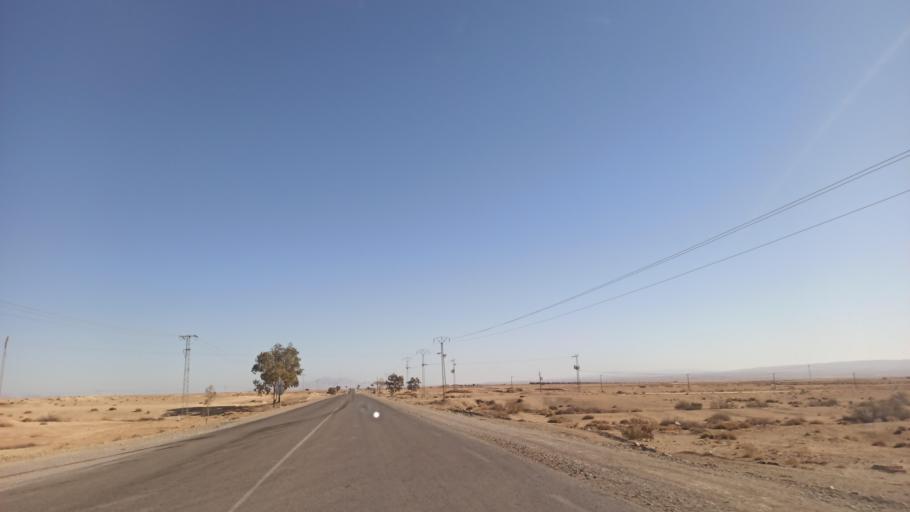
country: TN
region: Gafsa
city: Al Metlaoui
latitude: 34.3113
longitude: 8.4696
